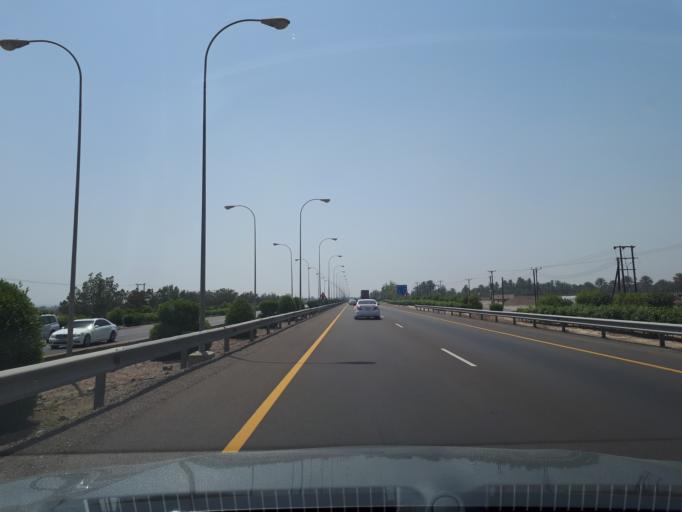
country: OM
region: Al Batinah
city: Al Sohar
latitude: 24.4046
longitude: 56.6562
